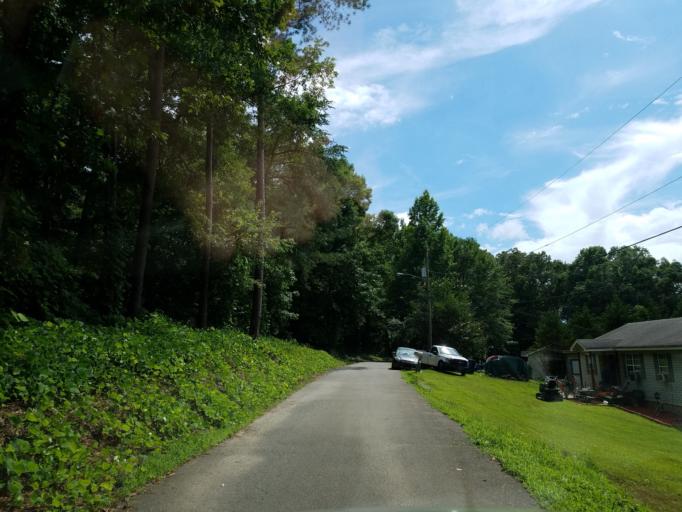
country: US
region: Georgia
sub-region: Cherokee County
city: Ball Ground
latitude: 34.3305
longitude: -84.3815
